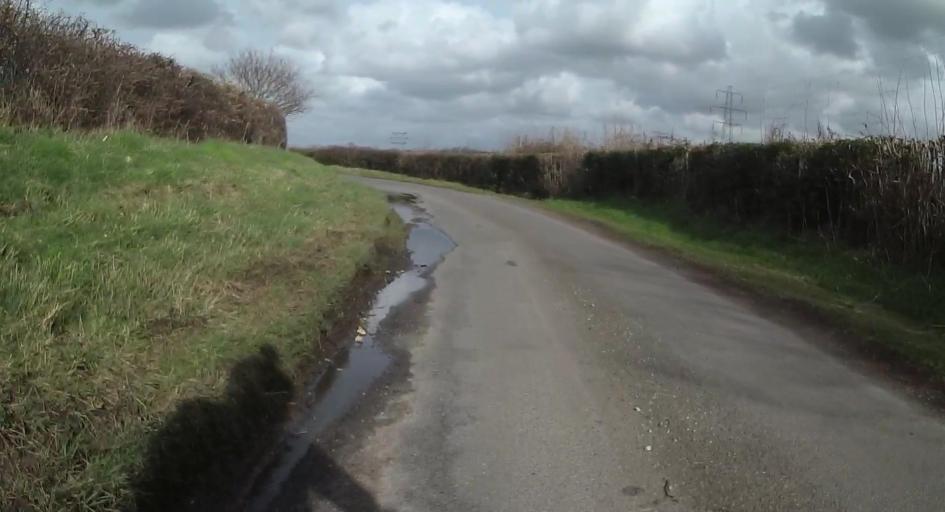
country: GB
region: England
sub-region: Hampshire
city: Kingsclere
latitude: 51.3389
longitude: -1.2428
